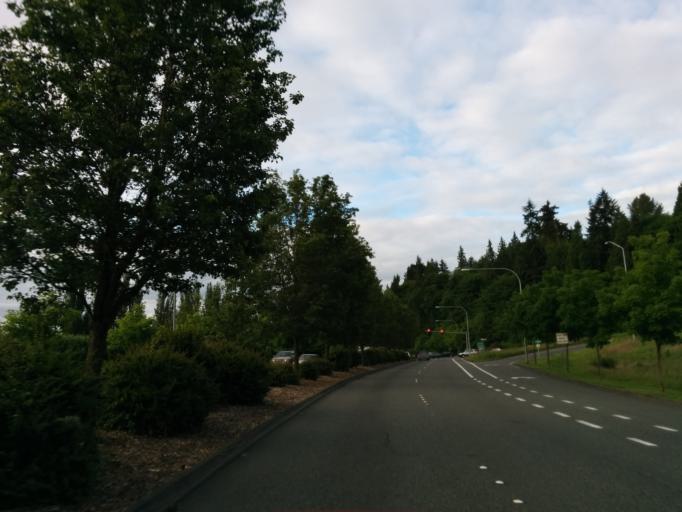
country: US
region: Washington
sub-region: King County
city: Redmond
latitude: 47.6665
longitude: -122.1269
